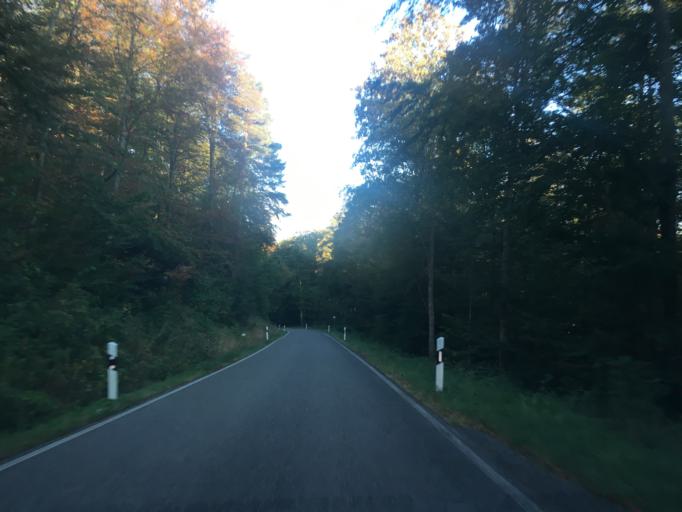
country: DE
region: Baden-Wuerttemberg
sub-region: Tuebingen Region
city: Pfullingen
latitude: 48.4009
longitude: 9.2512
